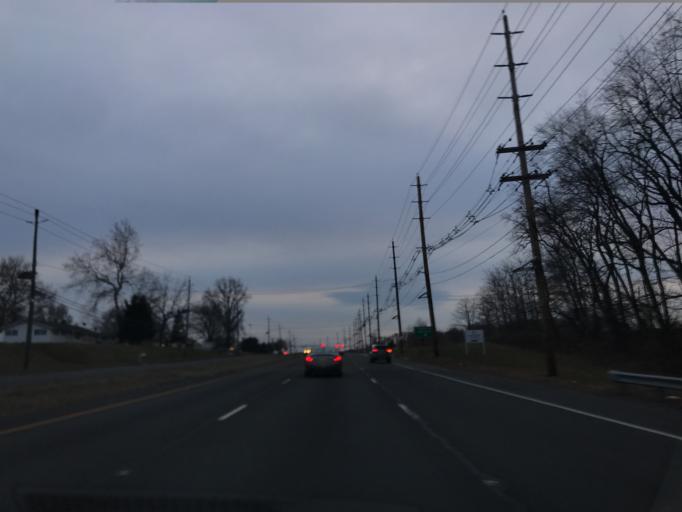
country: US
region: New Jersey
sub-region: Middlesex County
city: Milltown
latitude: 40.4311
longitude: -74.4910
